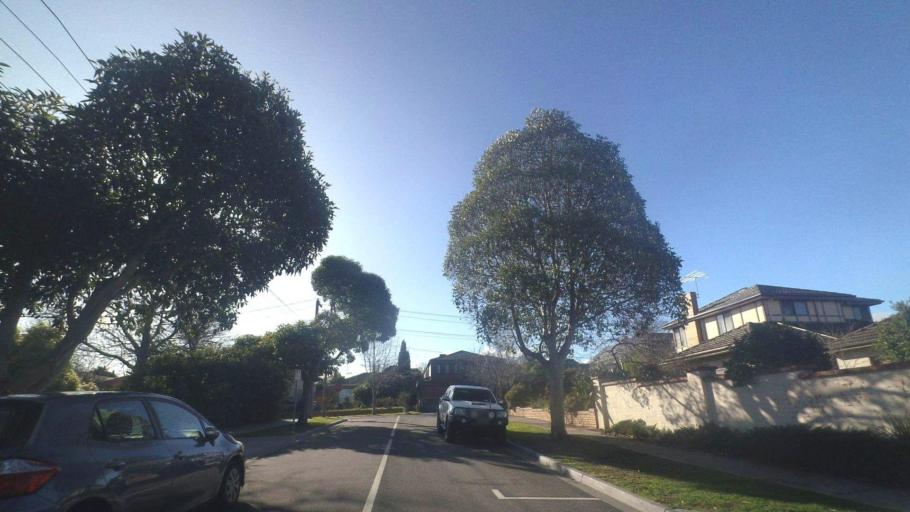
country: AU
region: Victoria
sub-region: Boroondara
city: Balwyn North
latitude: -37.7973
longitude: 145.0783
